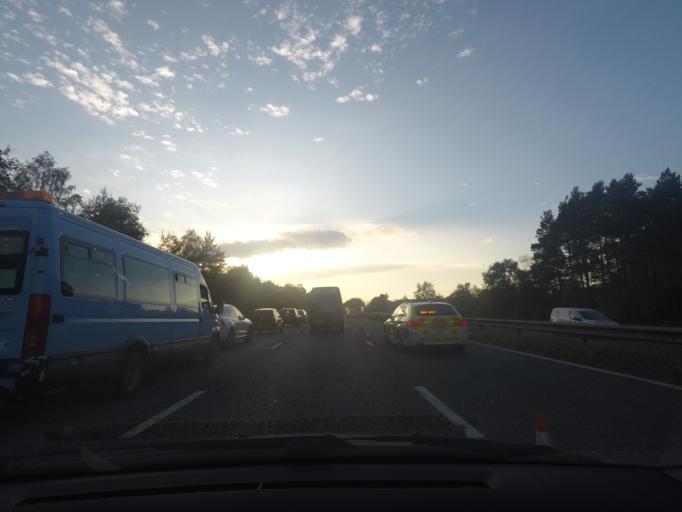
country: GB
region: England
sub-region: North Lincolnshire
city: Worlaby
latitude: 53.5799
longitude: -0.4455
